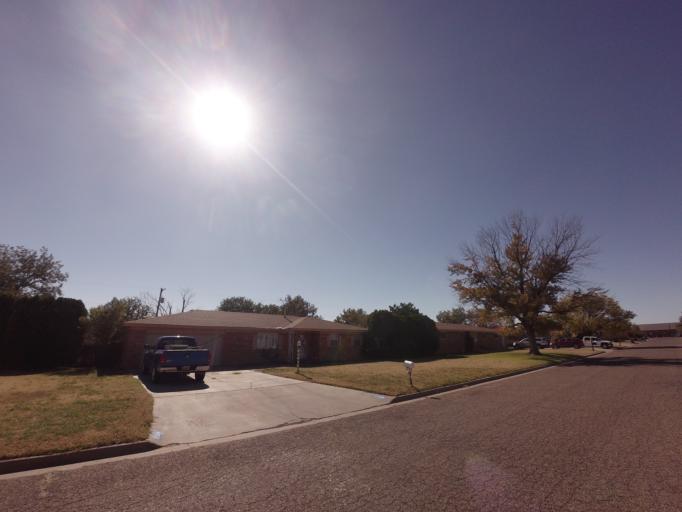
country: US
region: New Mexico
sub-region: Curry County
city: Clovis
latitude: 34.4207
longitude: -103.1921
